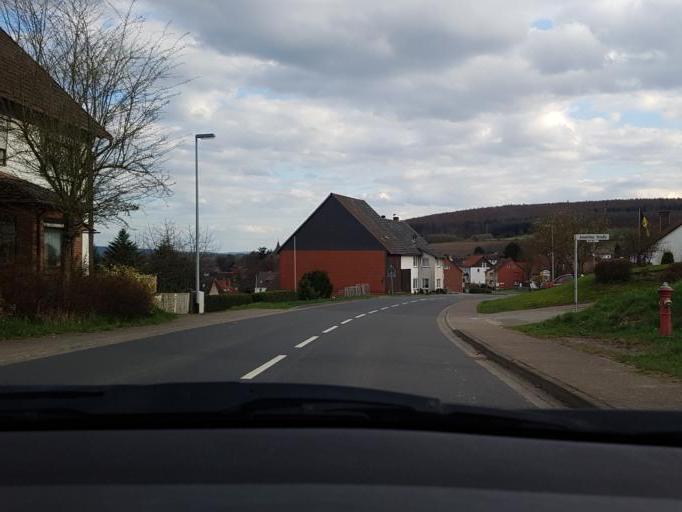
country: DE
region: Lower Saxony
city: Bodenfelde
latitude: 51.6927
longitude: 9.5547
